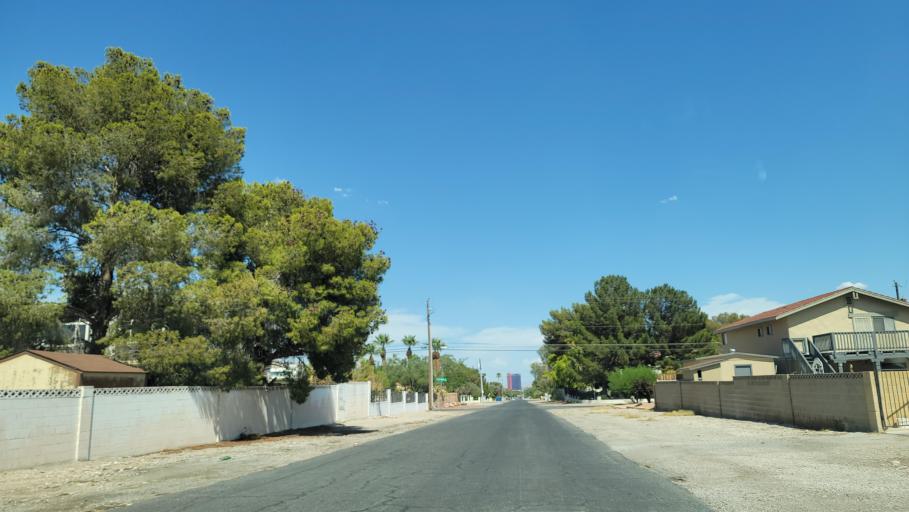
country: US
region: Nevada
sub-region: Clark County
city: Spring Valley
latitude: 36.1350
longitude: -115.2417
